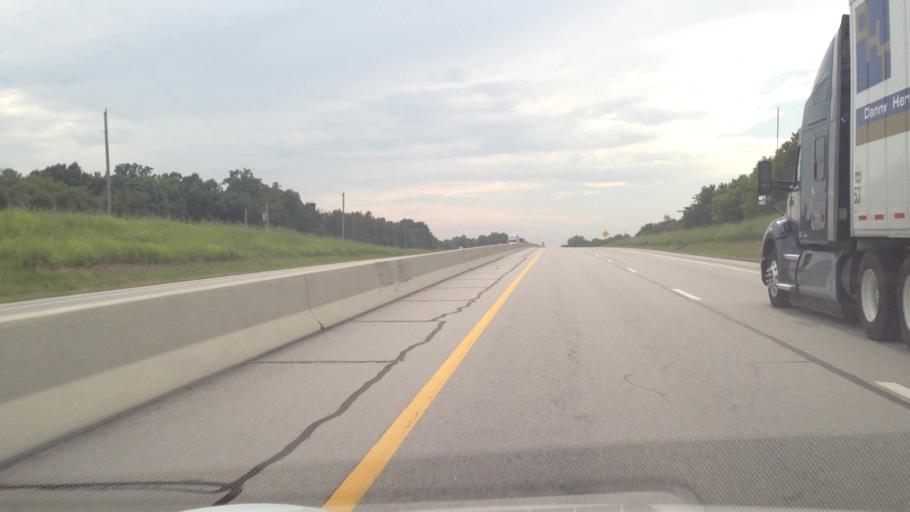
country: US
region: Kansas
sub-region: Cherokee County
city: Baxter Springs
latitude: 36.9246
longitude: -94.7463
